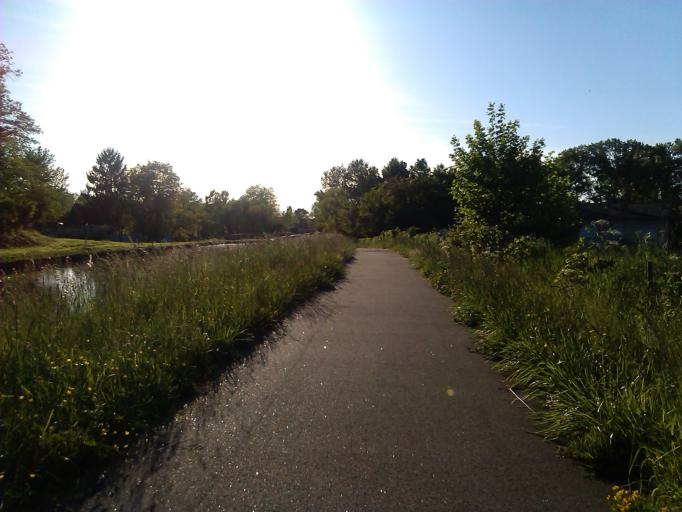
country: FR
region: Auvergne
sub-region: Departement de l'Allier
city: Dompierre-sur-Besbre
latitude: 46.5373
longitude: 3.7117
